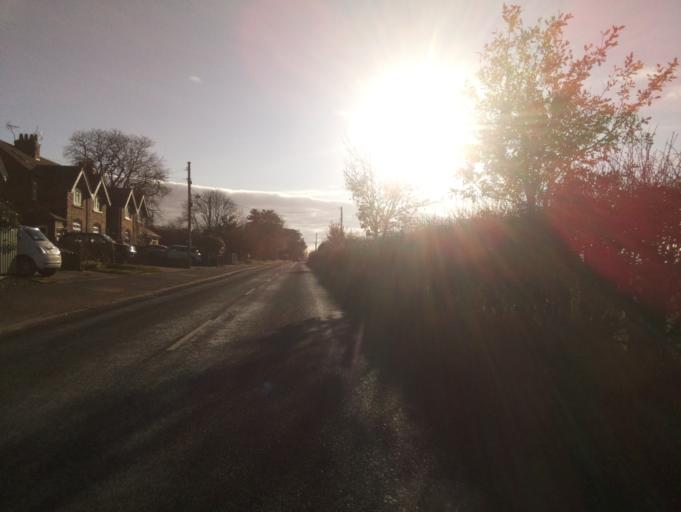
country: GB
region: England
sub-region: Derbyshire
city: Etwall
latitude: 52.8674
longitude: -1.6013
